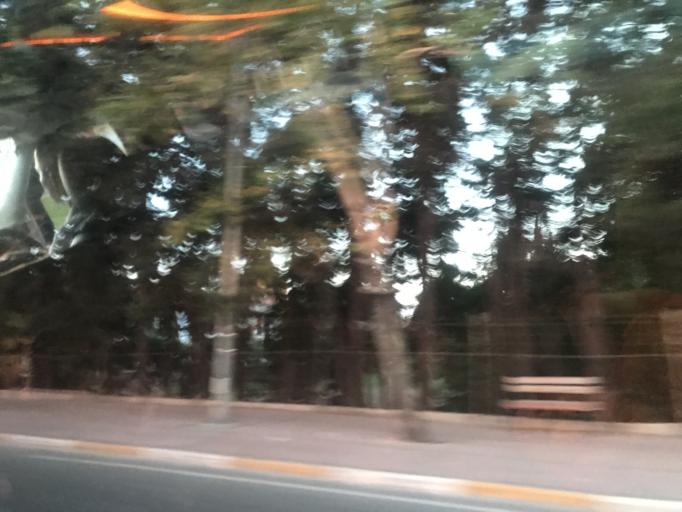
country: TR
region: Antalya
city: Antalya
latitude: 36.9148
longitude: 30.6757
